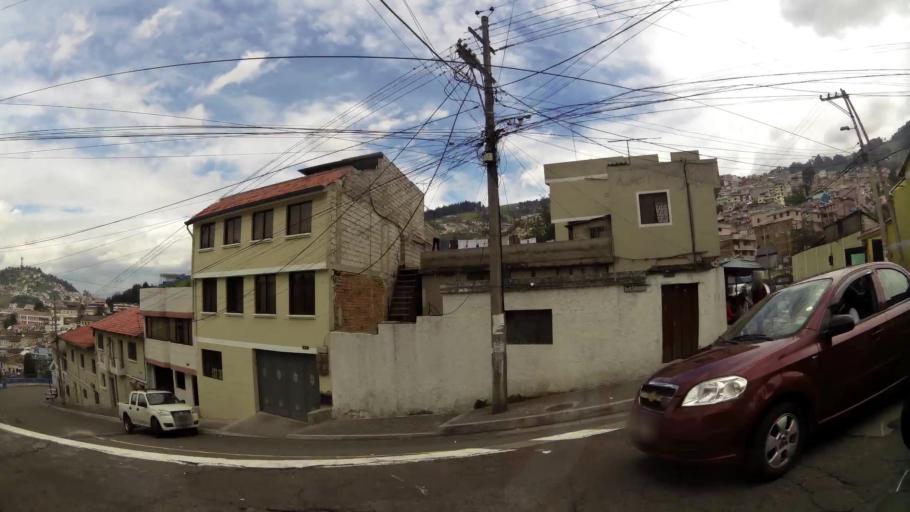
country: EC
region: Pichincha
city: Quito
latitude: -0.2126
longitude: -78.5161
